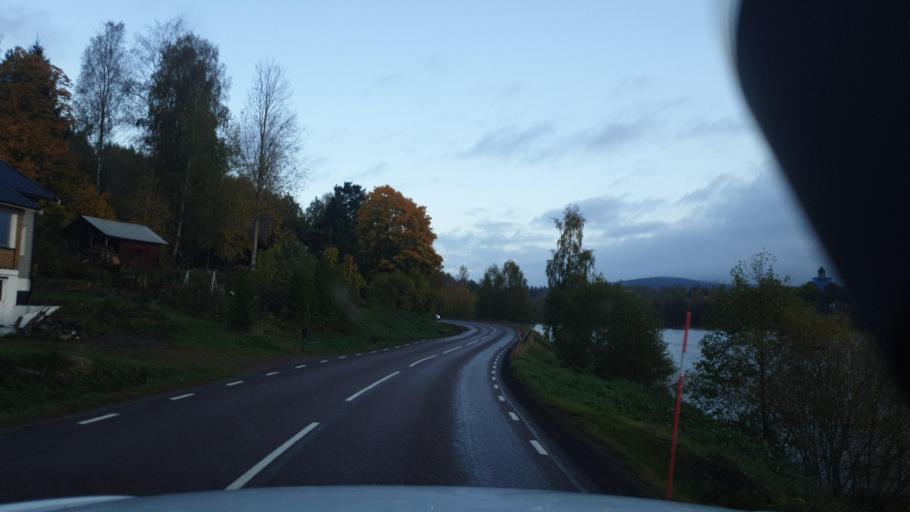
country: SE
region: Vaermland
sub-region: Arvika Kommun
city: Arvika
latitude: 59.8068
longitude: 12.5595
